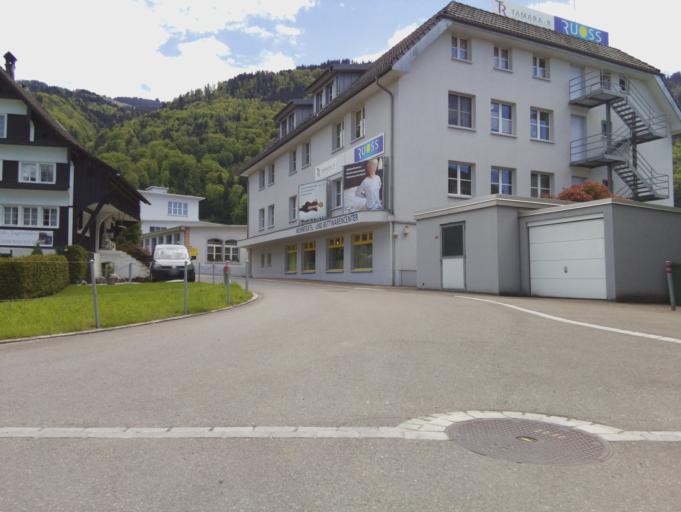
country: CH
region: Schwyz
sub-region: Bezirk March
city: Schubelbach
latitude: 47.1732
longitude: 8.9297
